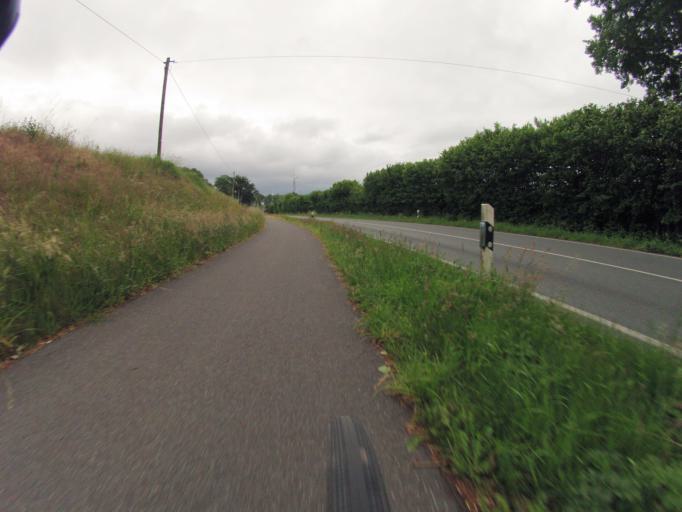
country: DE
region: North Rhine-Westphalia
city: Emsdetten
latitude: 52.2087
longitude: 7.5588
